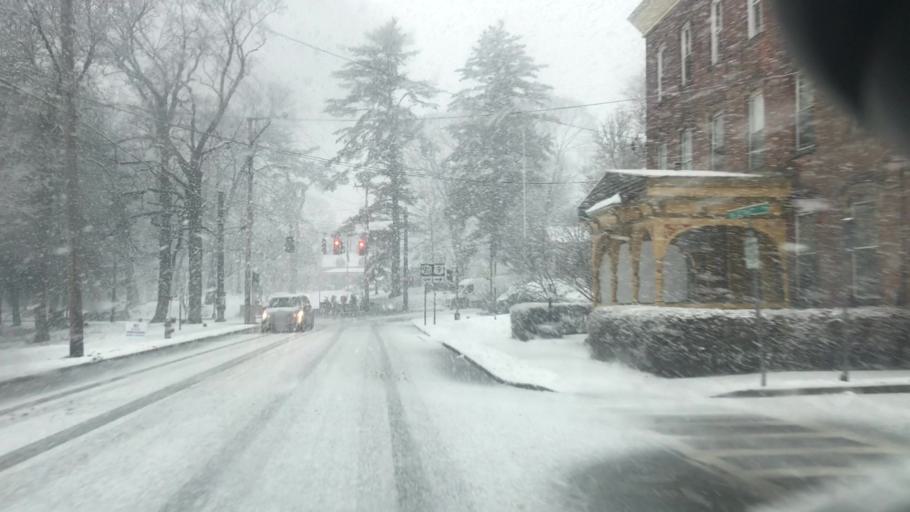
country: US
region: New York
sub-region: Dutchess County
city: Wappingers Falls
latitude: 41.5967
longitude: -73.9179
